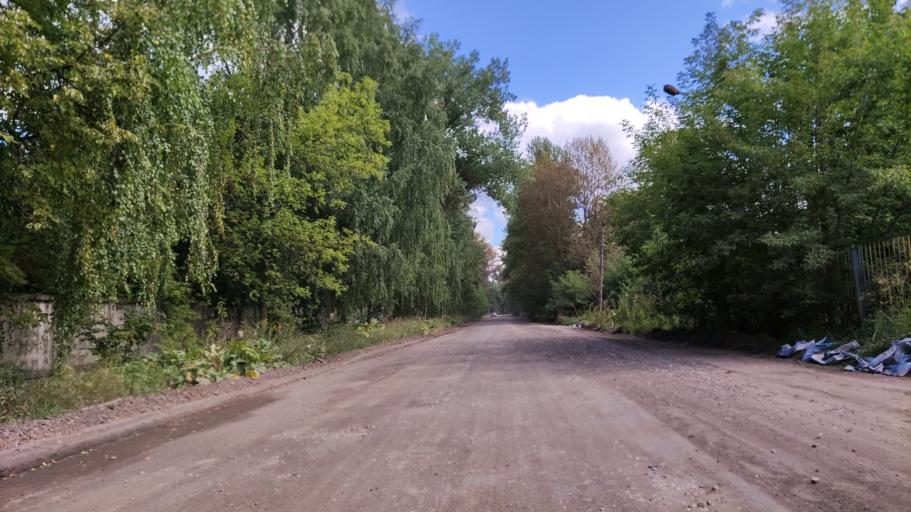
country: RU
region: Tverskaya
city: Rzhev
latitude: 56.2400
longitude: 34.3150
